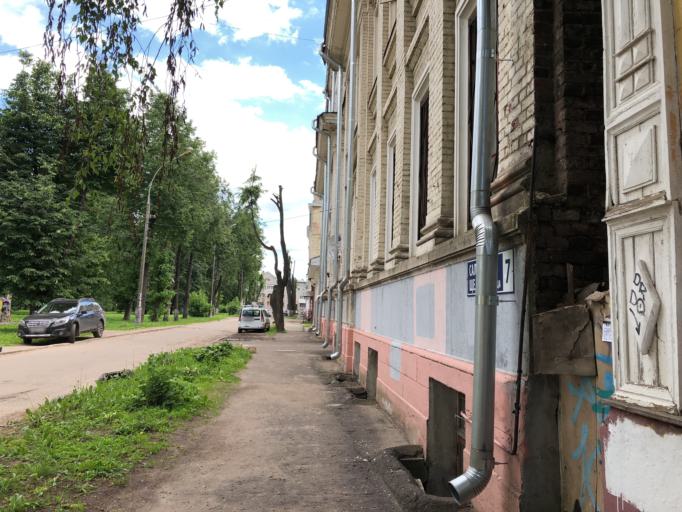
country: RU
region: Jaroslavl
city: Yaroslavl
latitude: 57.6235
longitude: 39.8742
